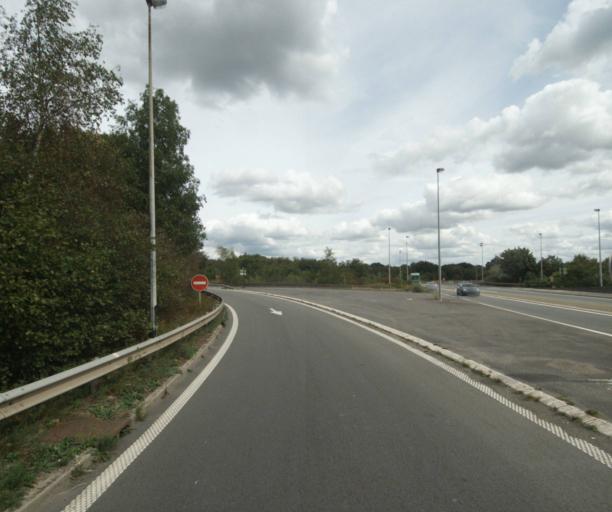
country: FR
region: Nord-Pas-de-Calais
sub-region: Departement du Pas-de-Calais
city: Oignies
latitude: 50.4850
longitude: 2.9826
